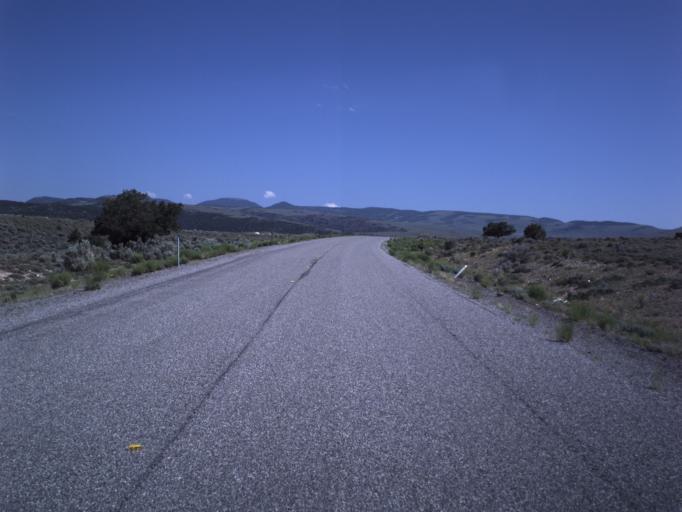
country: US
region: Utah
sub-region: Wayne County
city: Loa
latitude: 38.4958
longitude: -111.5351
